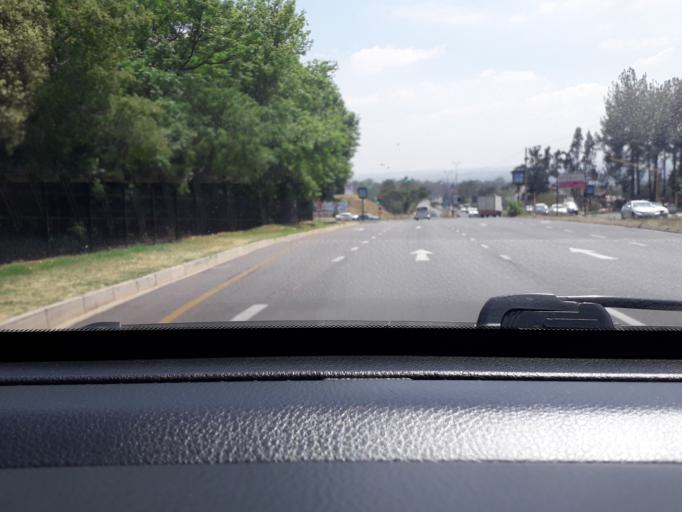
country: ZA
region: Gauteng
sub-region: City of Johannesburg Metropolitan Municipality
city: Diepsloot
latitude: -26.0406
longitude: 28.0253
